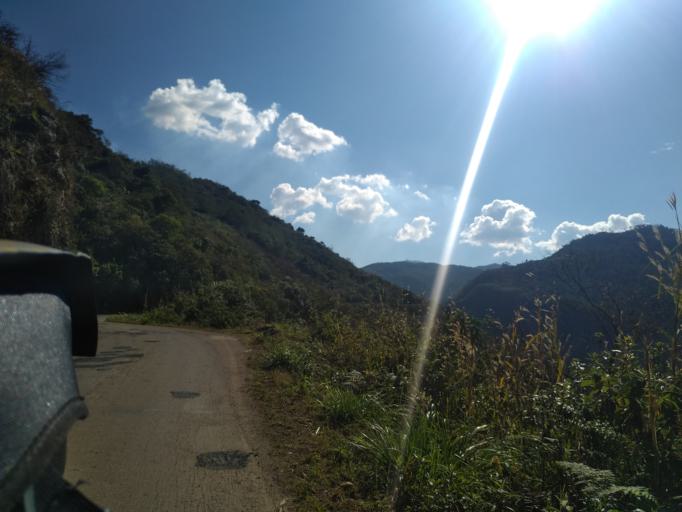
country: PE
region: Amazonas
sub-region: Provincia de Chachapoyas
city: Montevideo
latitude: -6.7142
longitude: -77.8138
